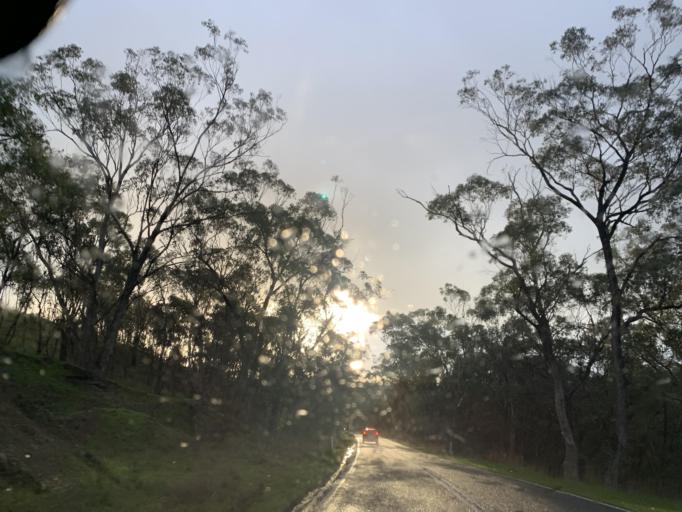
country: AU
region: Victoria
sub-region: Murrindindi
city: Kinglake West
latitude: -37.2106
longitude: 145.0906
